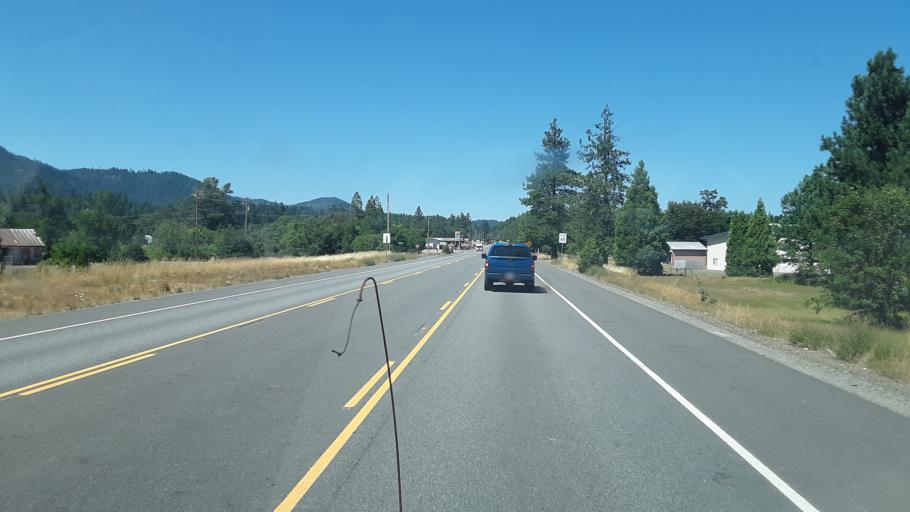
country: US
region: Oregon
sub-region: Josephine County
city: Cave Junction
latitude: 42.2757
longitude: -123.6173
